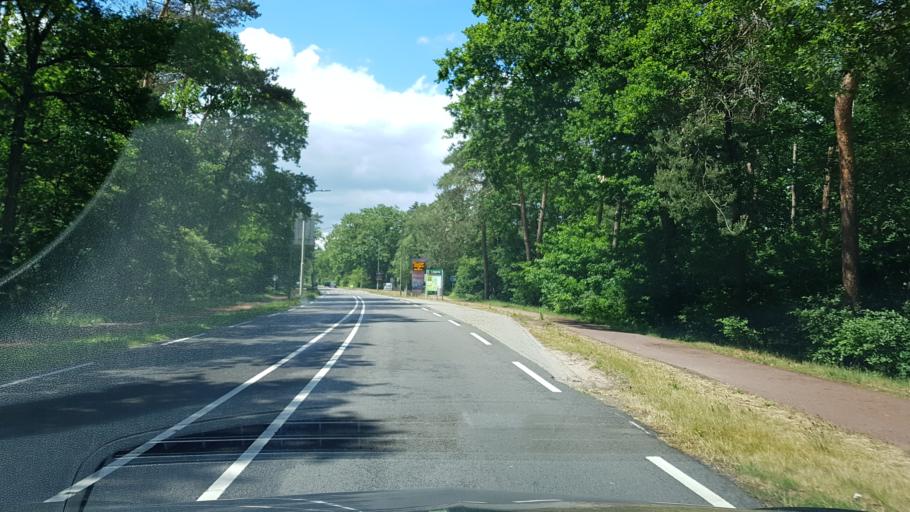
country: NL
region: Gelderland
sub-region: Gemeente Nunspeet
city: Nunspeet
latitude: 52.3786
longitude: 5.8109
